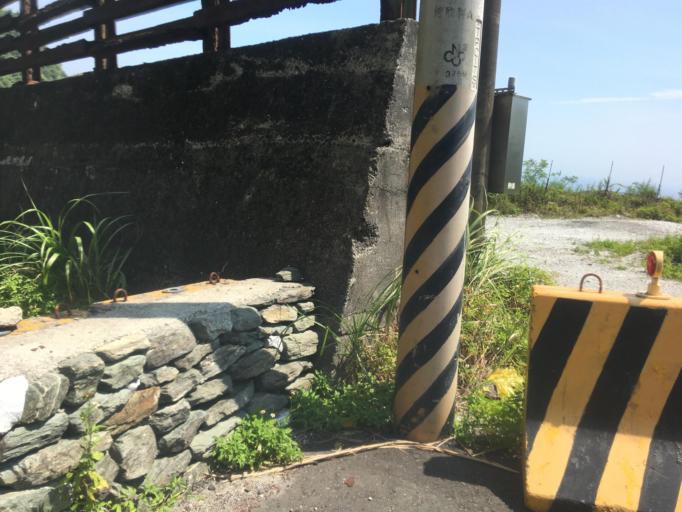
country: TW
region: Taiwan
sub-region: Yilan
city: Yilan
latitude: 24.5421
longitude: 121.8674
